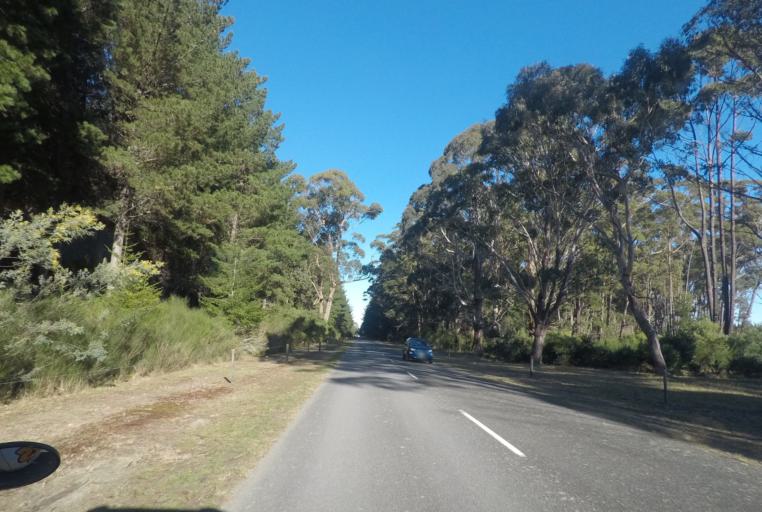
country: NZ
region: Tasman
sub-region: Tasman District
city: Mapua
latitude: -41.2681
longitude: 173.1517
